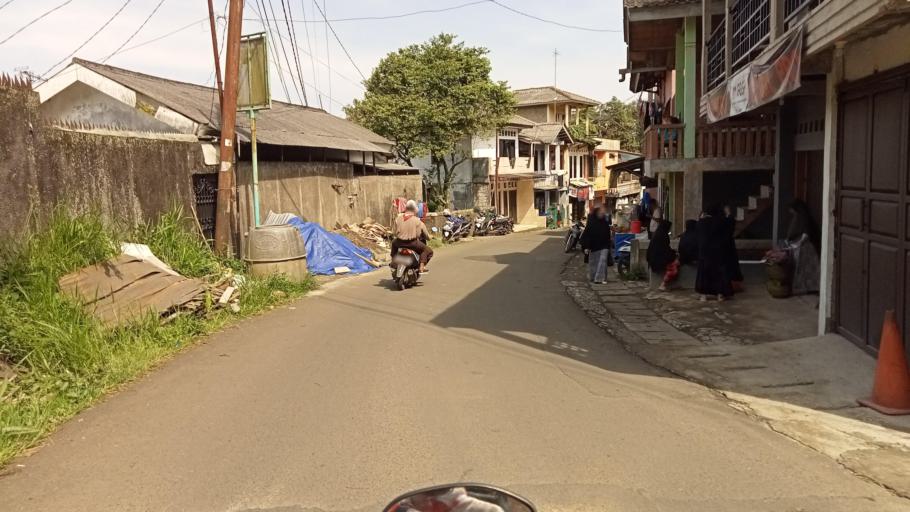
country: ID
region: West Java
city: Caringin
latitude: -6.6484
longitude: 106.9082
